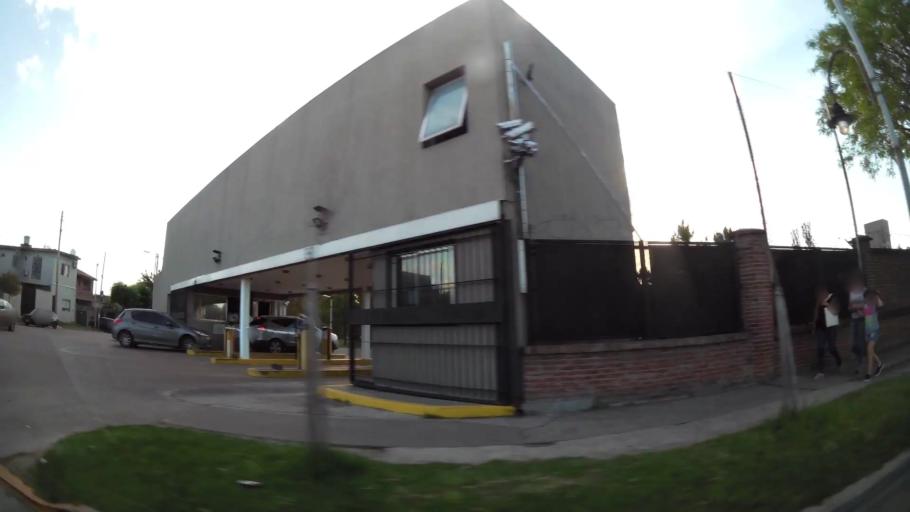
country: AR
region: Buenos Aires
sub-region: Partido de Tigre
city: Tigre
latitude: -34.4591
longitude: -58.5735
